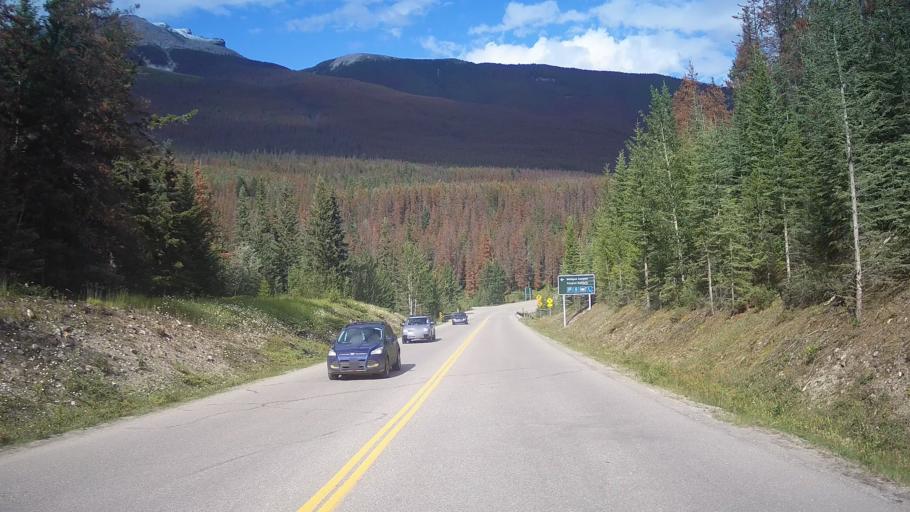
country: CA
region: Alberta
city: Jasper Park Lodge
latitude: 52.9188
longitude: -117.9994
